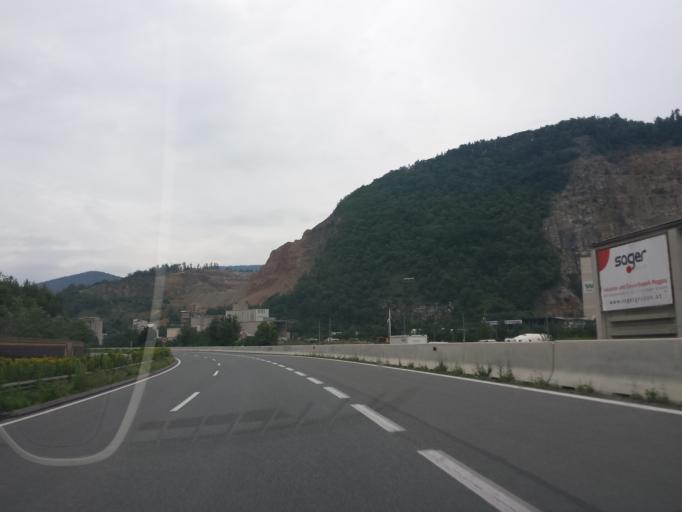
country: AT
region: Styria
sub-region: Politischer Bezirk Graz-Umgebung
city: Peggau
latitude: 47.2108
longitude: 15.3398
